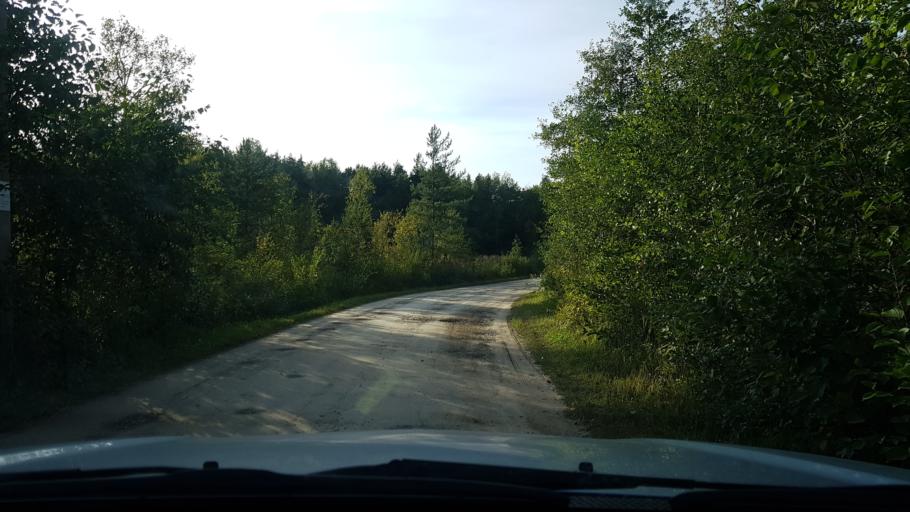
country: EE
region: Ida-Virumaa
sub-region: Sillamaee linn
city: Sillamae
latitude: 59.2592
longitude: 27.9253
